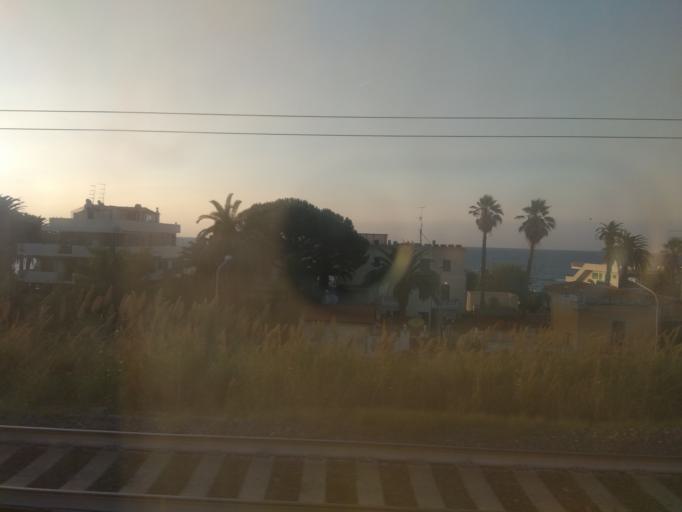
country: IT
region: Latium
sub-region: Citta metropolitana di Roma Capitale
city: Santa Marinella
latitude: 42.0353
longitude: 11.8589
